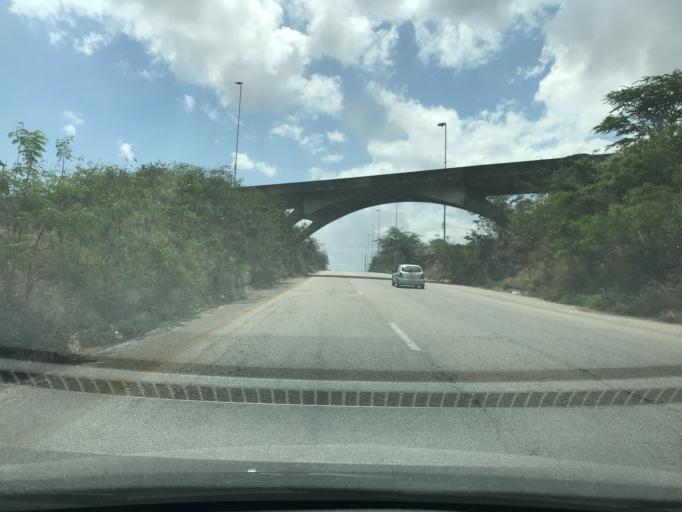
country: BR
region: Pernambuco
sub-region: Caruaru
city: Caruaru
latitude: -8.3060
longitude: -35.9642
